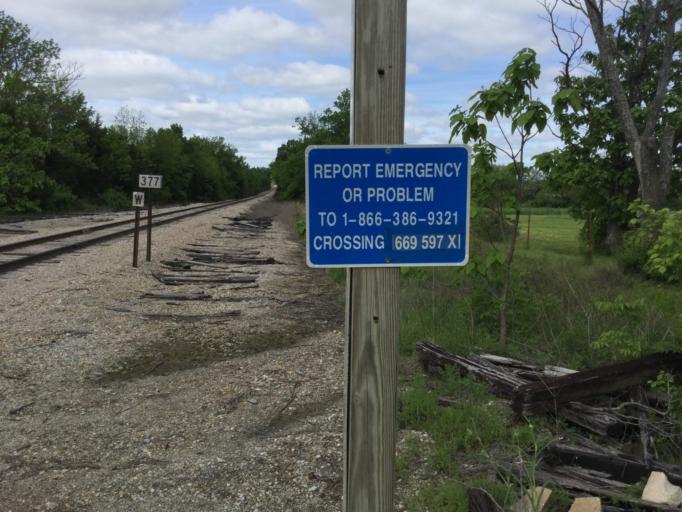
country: US
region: Kansas
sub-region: Labette County
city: Altamont
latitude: 37.2078
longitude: -95.4101
